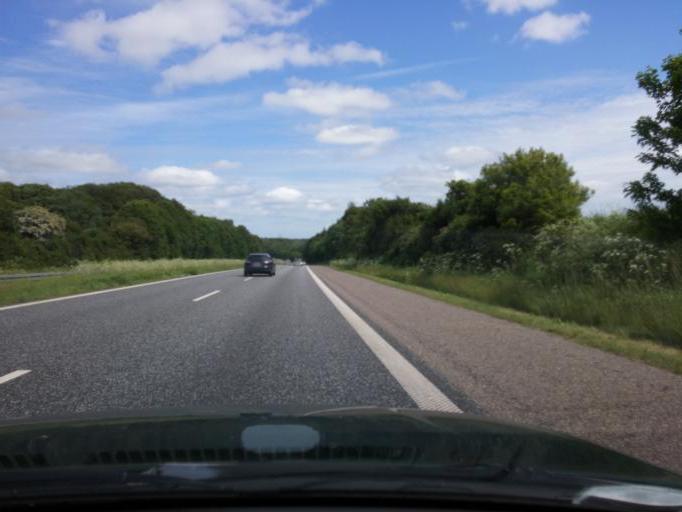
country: DK
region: South Denmark
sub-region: Fredericia Kommune
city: Taulov
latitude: 55.5460
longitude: 9.5396
